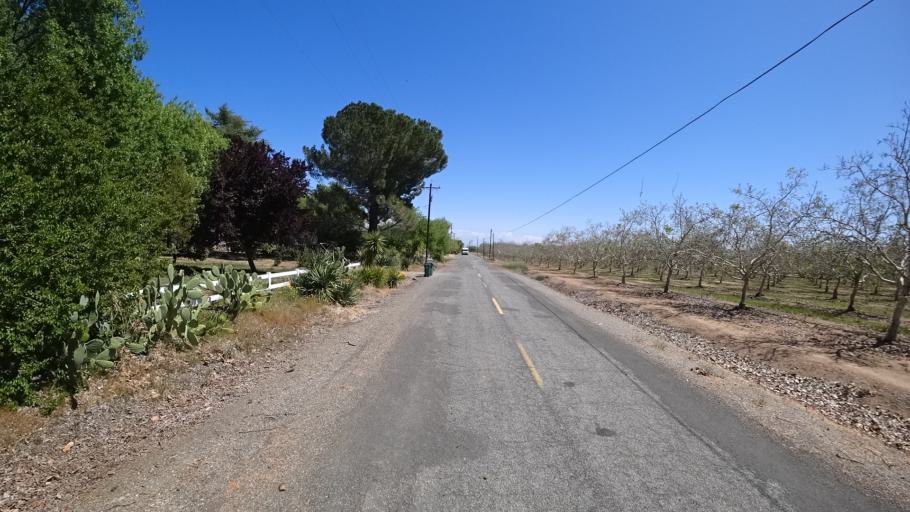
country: US
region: California
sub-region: Glenn County
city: Orland
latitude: 39.7894
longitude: -122.2124
